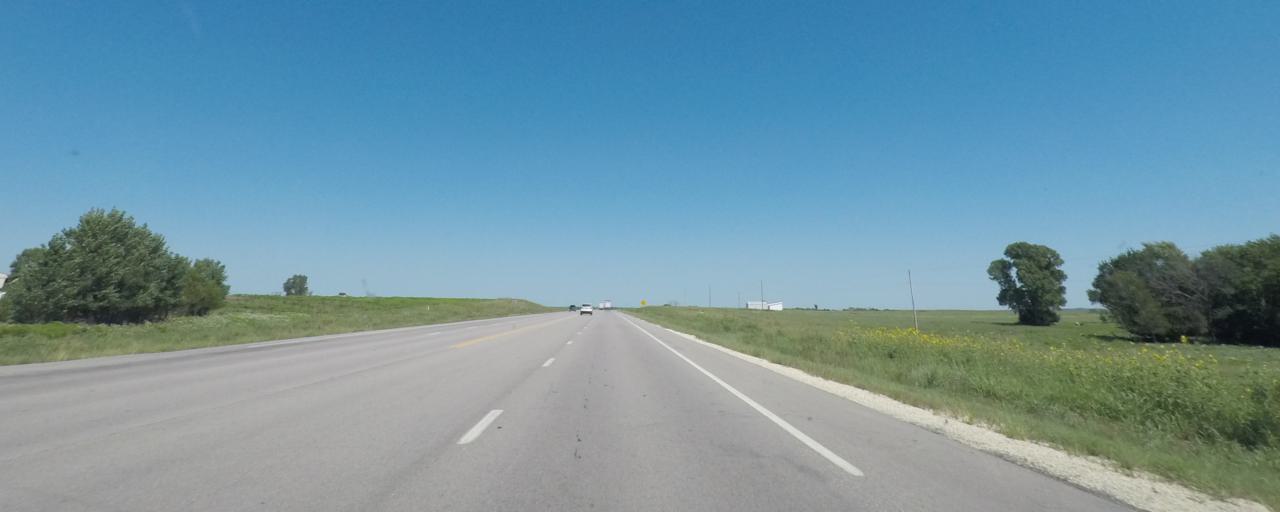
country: US
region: Kansas
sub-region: Chase County
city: Cottonwood Falls
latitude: 38.4016
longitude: -96.5021
